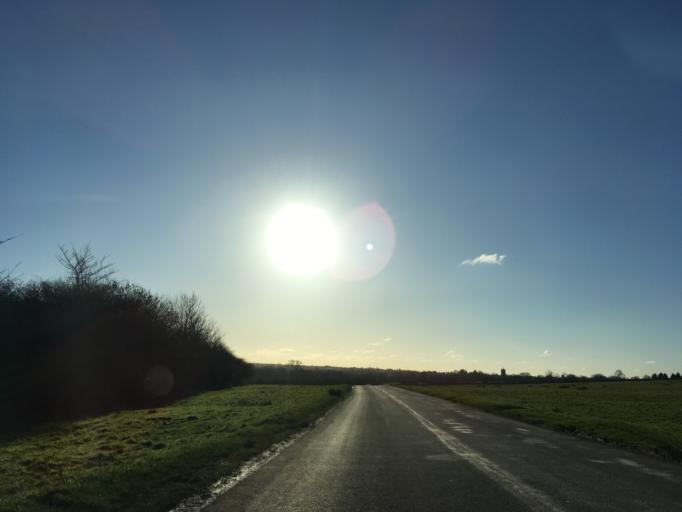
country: GB
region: England
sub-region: South Gloucestershire
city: Chipping Sodbury
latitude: 51.5492
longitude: -2.3795
